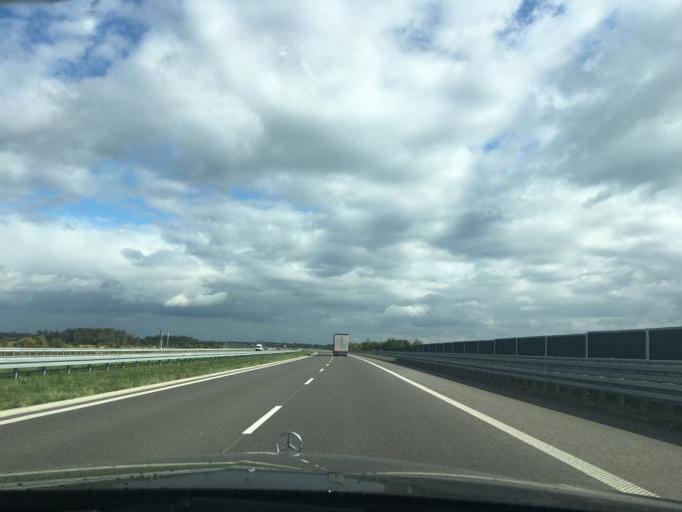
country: PL
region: Subcarpathian Voivodeship
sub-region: Powiat rzeszowski
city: Krasne
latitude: 50.0925
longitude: 22.0754
